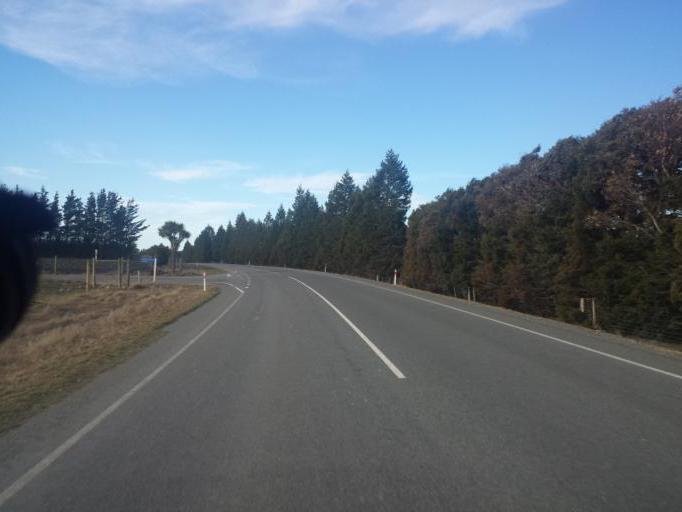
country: NZ
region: Canterbury
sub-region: Ashburton District
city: Methven
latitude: -43.6091
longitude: 171.5206
